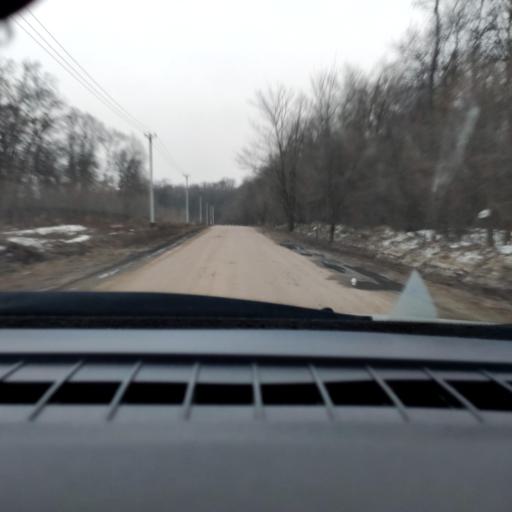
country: RU
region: Samara
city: Novosemeykino
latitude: 53.3316
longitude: 50.2733
